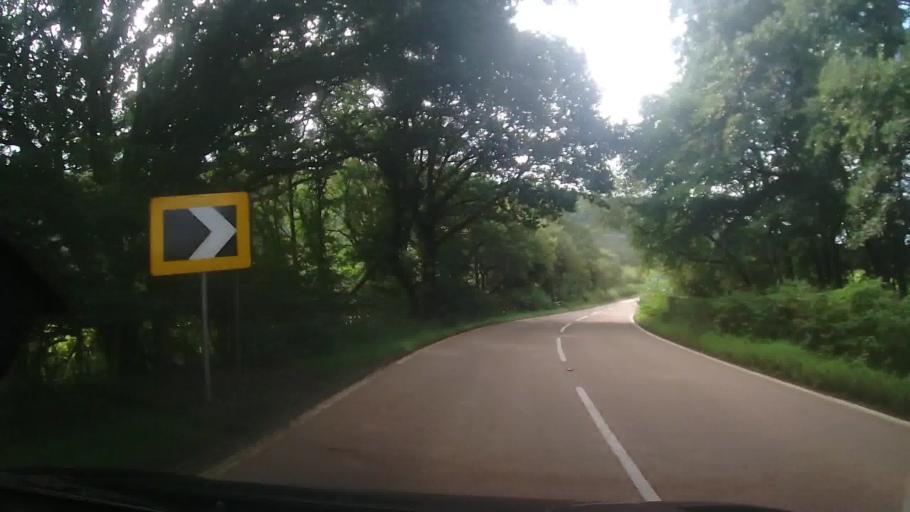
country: GB
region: Wales
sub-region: Sir Powys
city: Machynlleth
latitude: 52.5626
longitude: -3.9128
